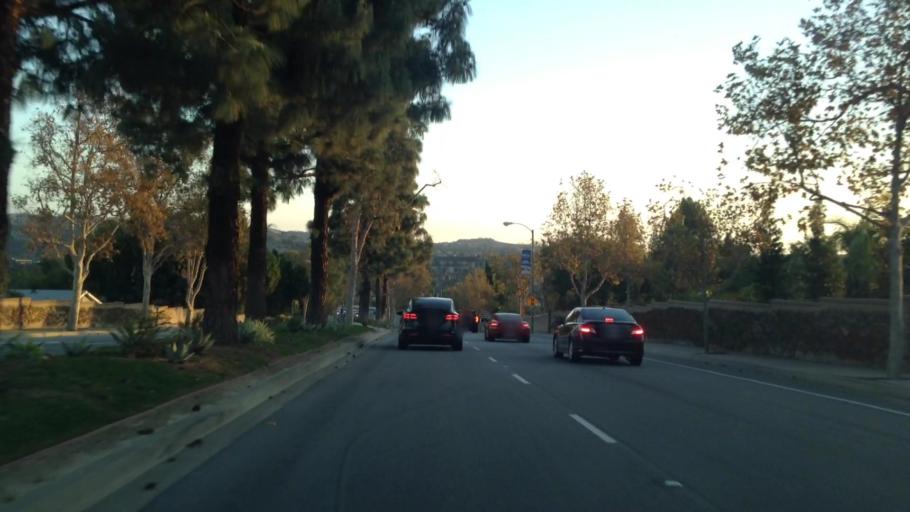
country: US
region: California
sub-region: Orange County
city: Yorba Linda
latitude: 33.8805
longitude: -117.7547
